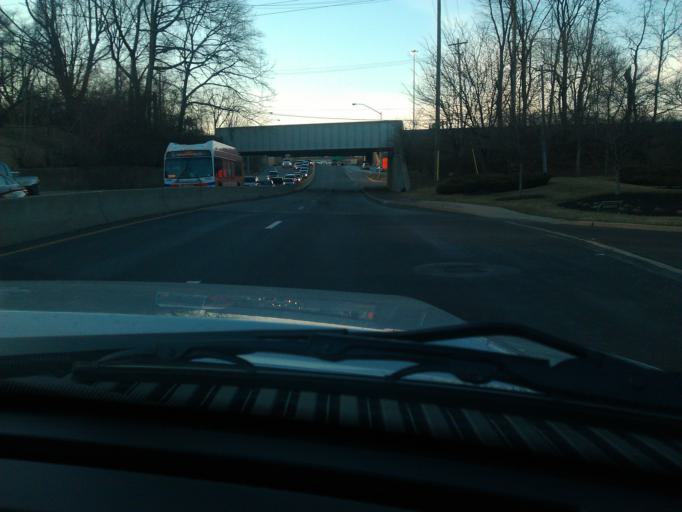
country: US
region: Pennsylvania
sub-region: Montgomery County
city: Plymouth Meeting
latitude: 40.1061
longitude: -75.2819
